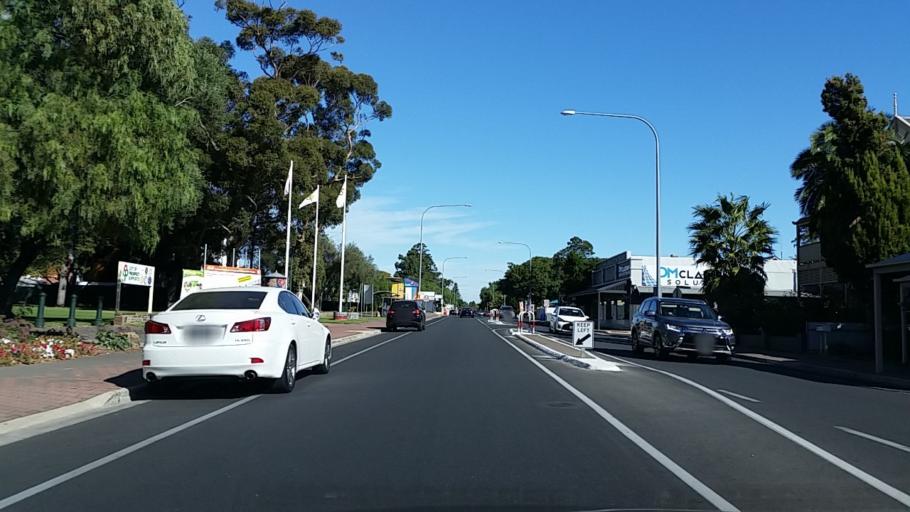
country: AU
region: South Australia
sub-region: Prospect
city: Prospect
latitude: -34.8922
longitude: 138.5944
